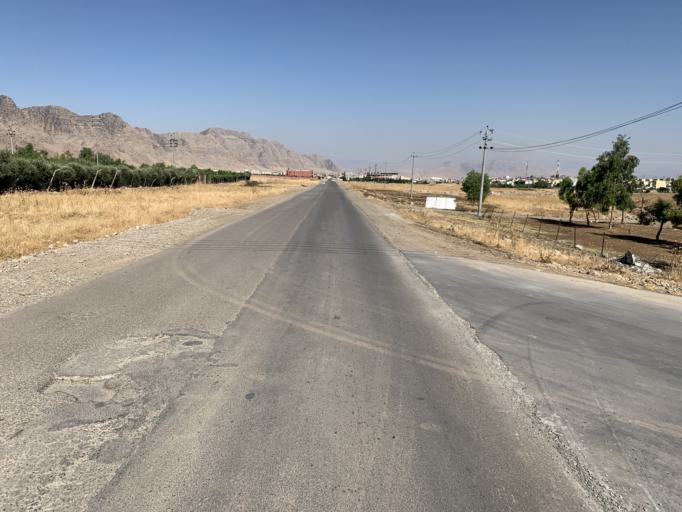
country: IQ
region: As Sulaymaniyah
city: Raniye
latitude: 36.2639
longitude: 44.8467
